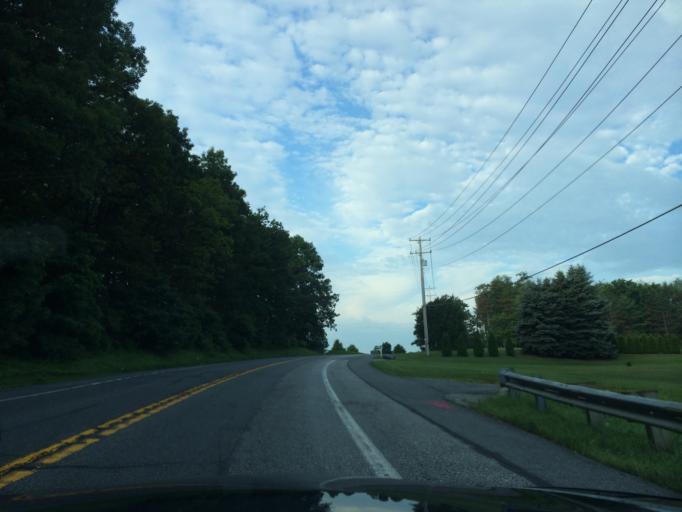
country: US
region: Maryland
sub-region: Carroll County
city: Mount Airy
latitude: 39.4233
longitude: -77.1095
